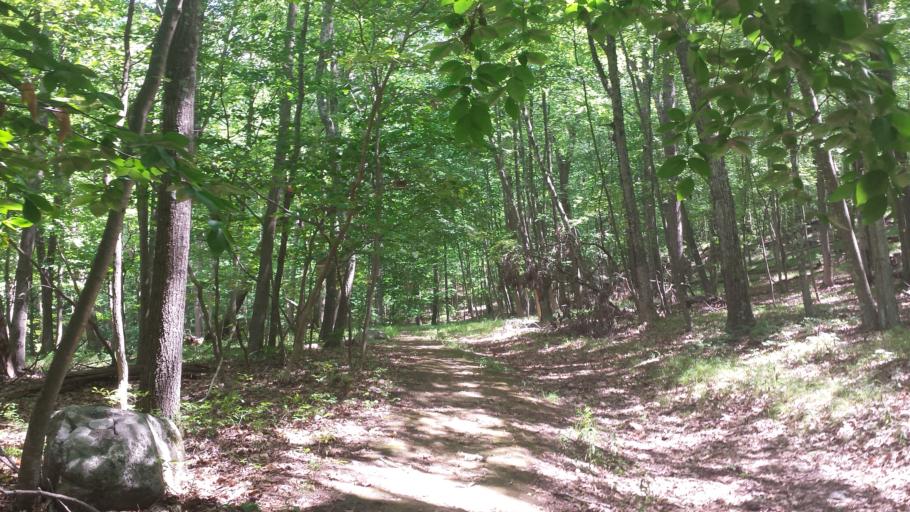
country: US
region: New York
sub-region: Westchester County
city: Pound Ridge
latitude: 41.2553
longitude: -73.5793
